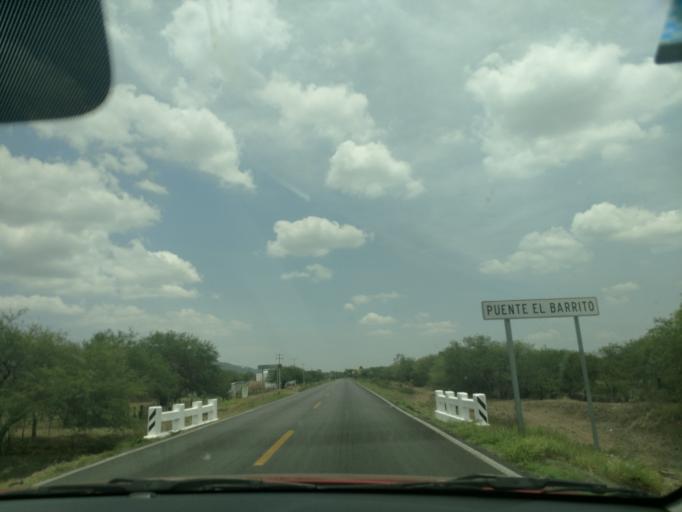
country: MX
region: San Luis Potosi
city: Villa Juarez
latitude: 22.0184
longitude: -100.3907
